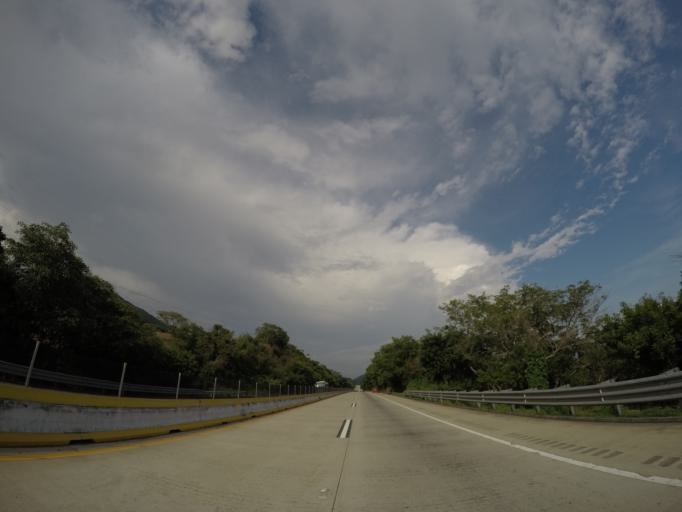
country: MX
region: Guerrero
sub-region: Acapulco de Juarez
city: Kilometro 30
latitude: 17.0011
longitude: -99.6844
